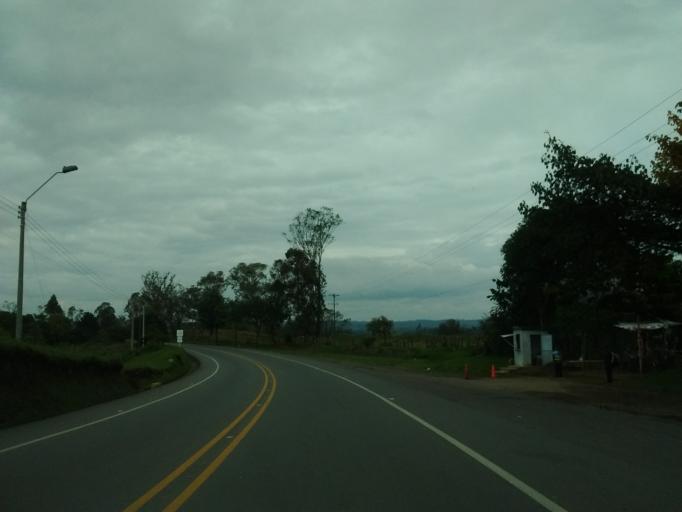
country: CO
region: Cauca
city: Popayan
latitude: 2.5152
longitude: -76.5422
